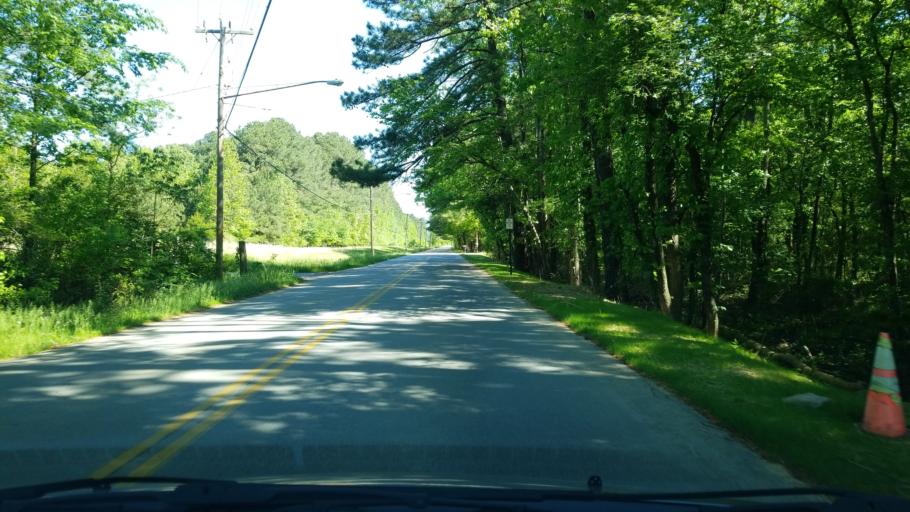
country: US
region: Tennessee
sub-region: Hamilton County
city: Chattanooga
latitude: 35.0359
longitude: -85.3347
